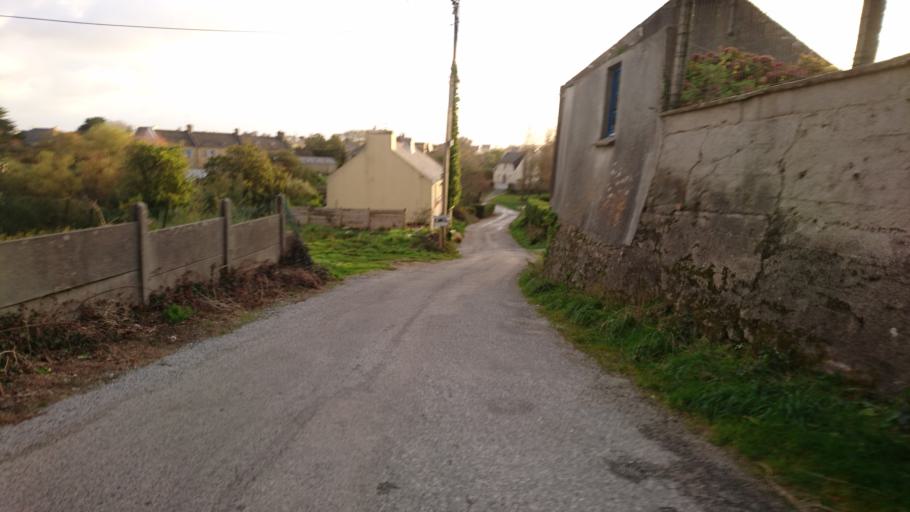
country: FR
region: Brittany
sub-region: Departement du Finistere
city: Lampaul-Plouarzel
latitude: 48.4392
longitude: -4.7732
